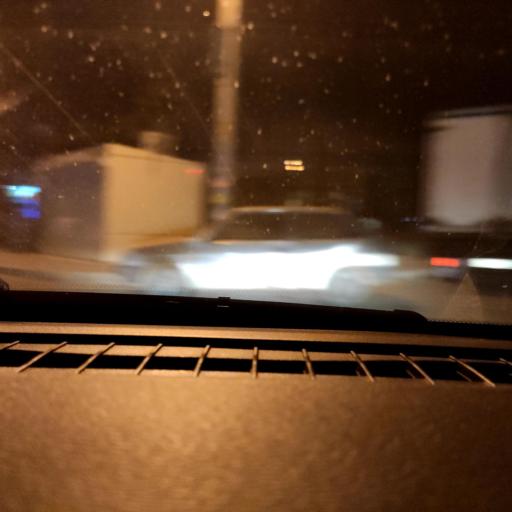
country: RU
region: Voronezj
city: Pridonskoy
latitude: 51.6865
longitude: 39.1094
